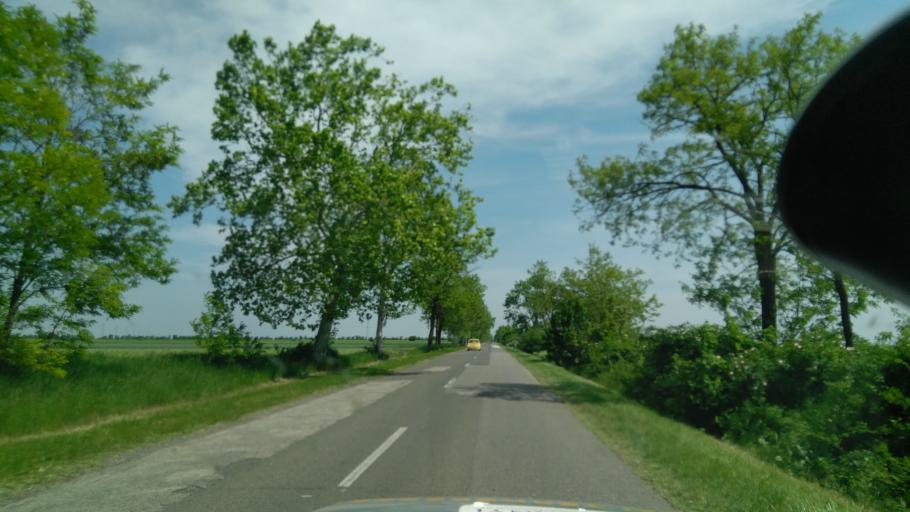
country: HU
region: Csongrad
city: Szekkutas
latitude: 46.5783
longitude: 20.4986
